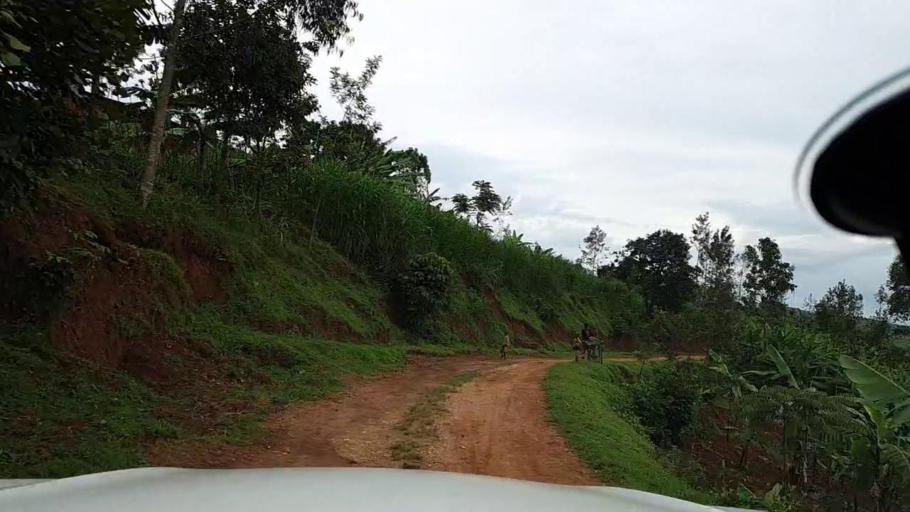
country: RW
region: Southern Province
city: Gitarama
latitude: -2.0887
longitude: 29.6359
